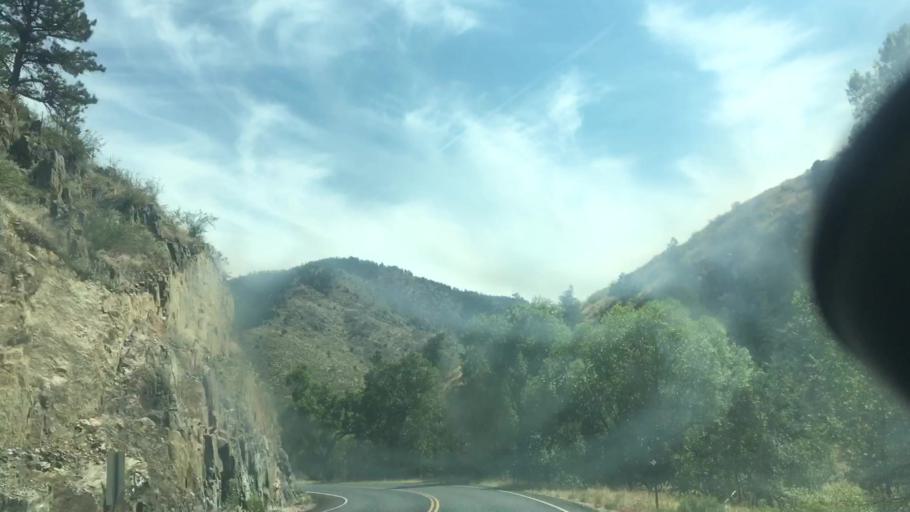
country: US
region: Colorado
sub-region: Larimer County
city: Laporte
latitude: 40.5613
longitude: -105.2999
